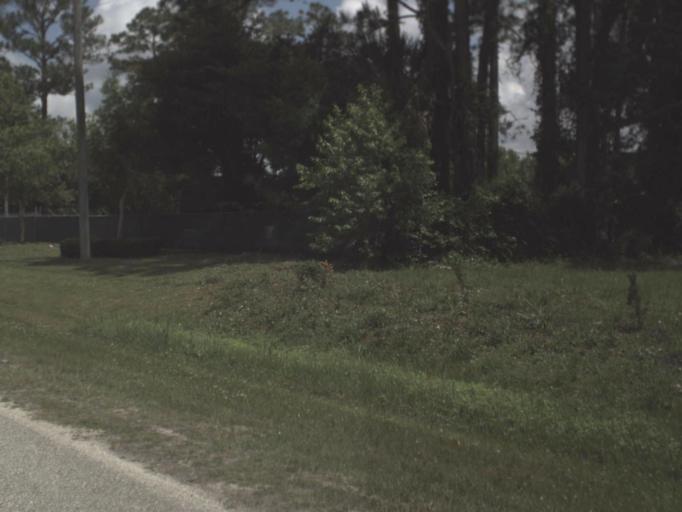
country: US
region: Florida
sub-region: Saint Johns County
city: Palm Valley
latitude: 30.0848
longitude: -81.4586
